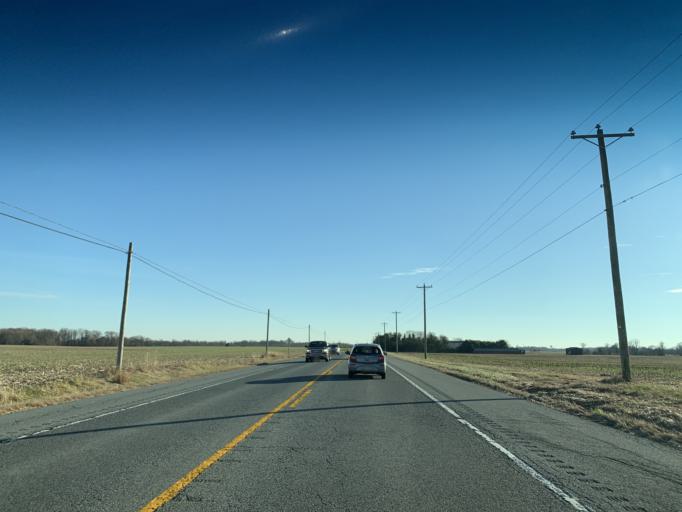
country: US
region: Delaware
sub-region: New Castle County
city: Middletown
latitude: 39.4374
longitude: -75.8619
